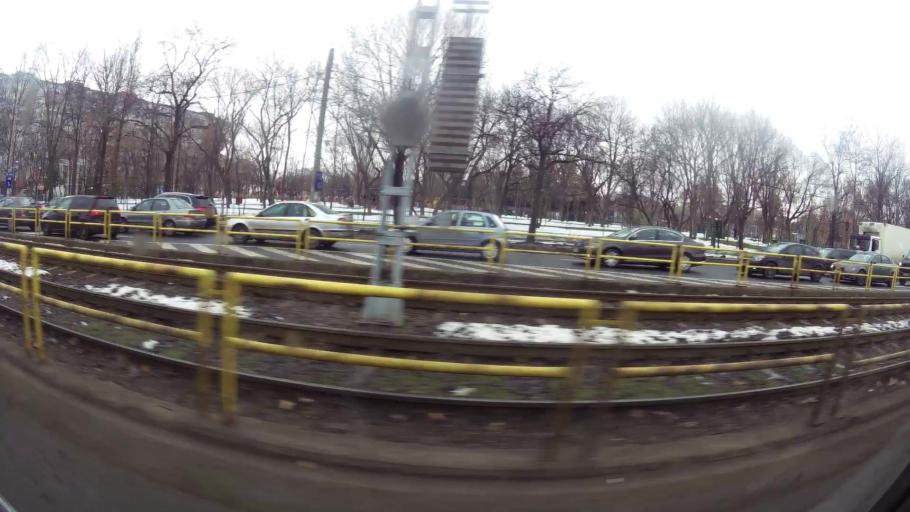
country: RO
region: Ilfov
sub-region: Comuna Chiajna
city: Rosu
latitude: 44.4189
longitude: 26.0345
